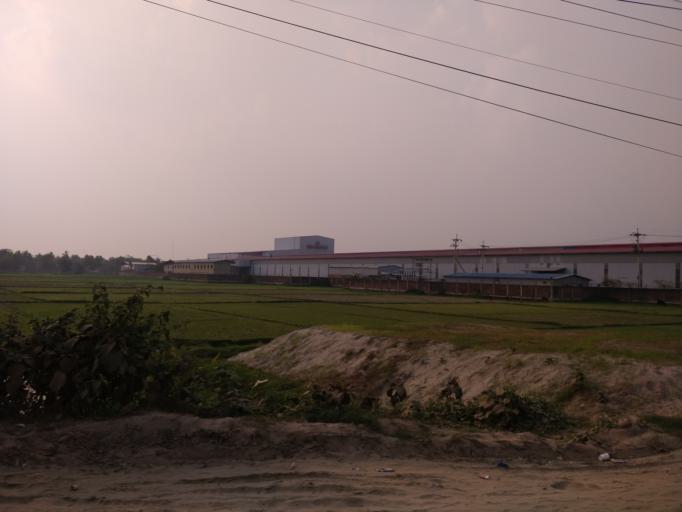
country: BD
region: Sylhet
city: Habiganj
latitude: 24.1506
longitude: 91.3478
